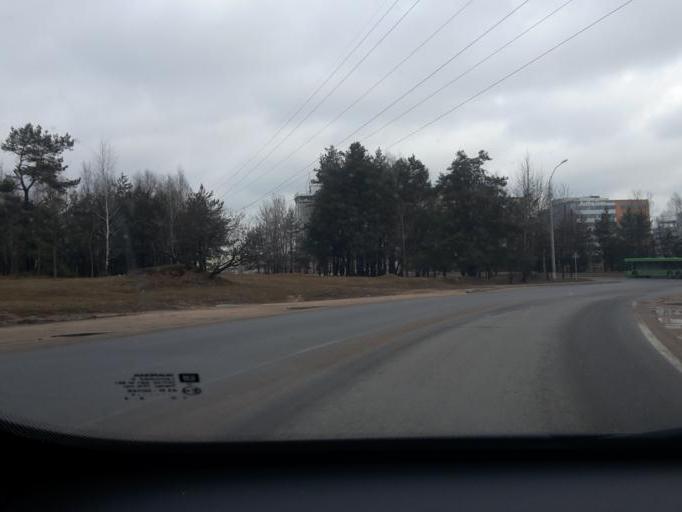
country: BY
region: Minsk
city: Borovlyany
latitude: 53.9240
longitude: 27.6811
